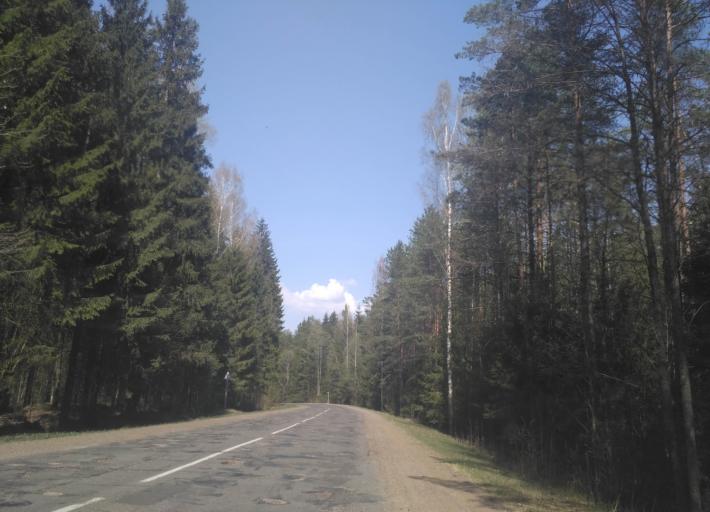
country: BY
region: Minsk
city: Loshnitsa
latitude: 54.4395
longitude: 28.6489
